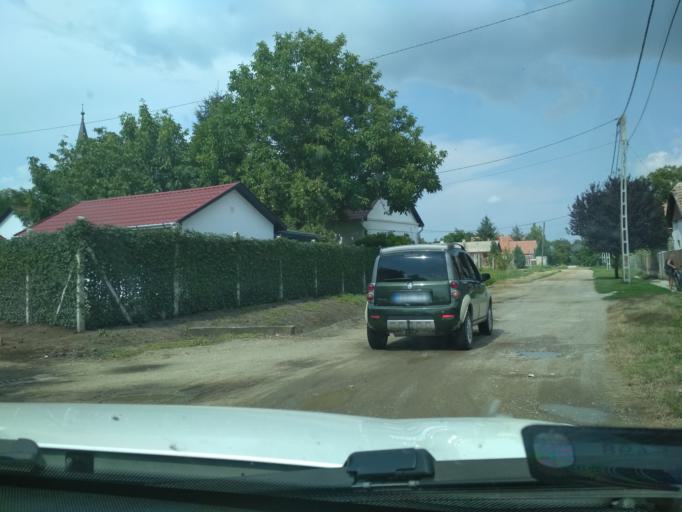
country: HU
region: Jasz-Nagykun-Szolnok
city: Abadszalok
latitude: 47.4765
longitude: 20.5867
